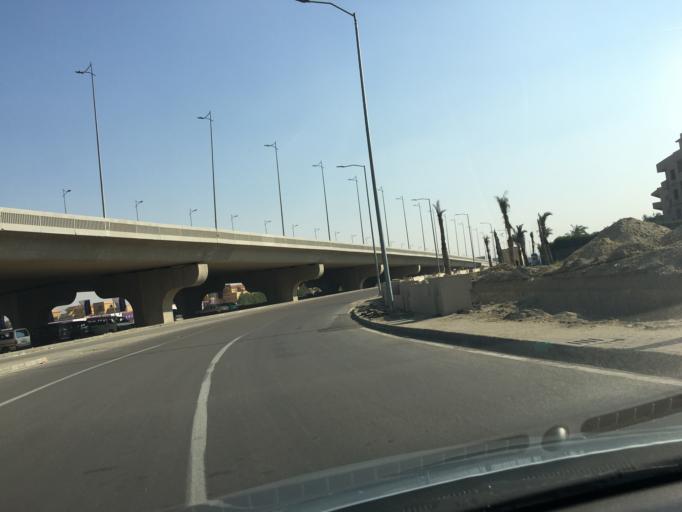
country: EG
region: Al Jizah
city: Awsim
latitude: 30.0078
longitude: 30.9819
